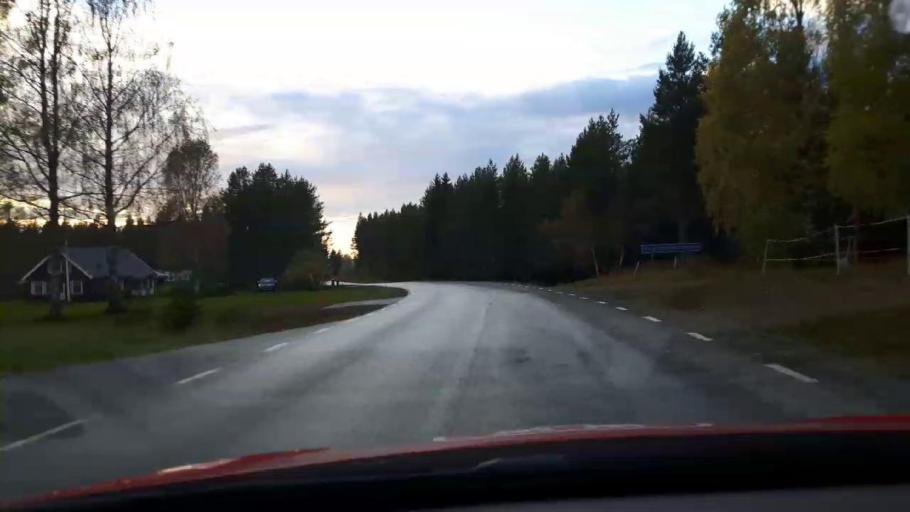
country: SE
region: Jaemtland
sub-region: OEstersunds Kommun
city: Lit
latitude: 63.3114
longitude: 15.1177
